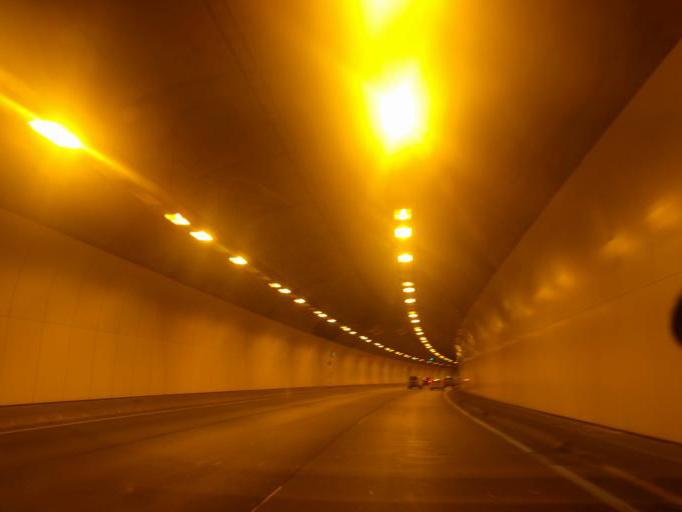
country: AU
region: South Australia
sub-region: Burnside
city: Mount Osmond
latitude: -34.9767
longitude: 138.6793
